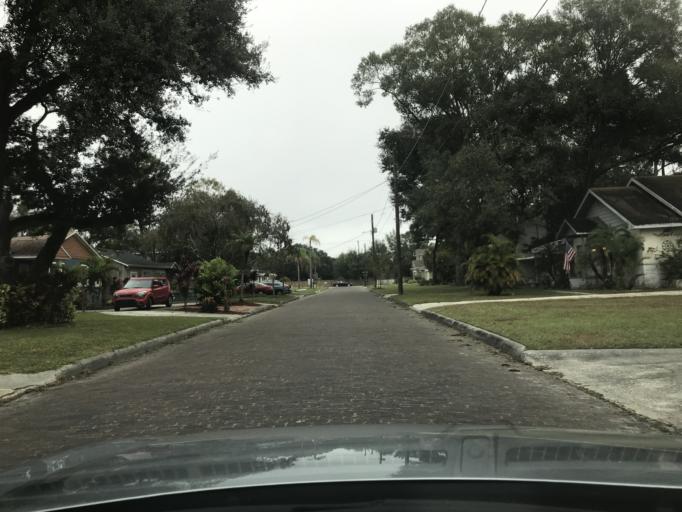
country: US
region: Florida
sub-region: Hillsborough County
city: Tampa
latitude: 27.9763
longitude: -82.4691
